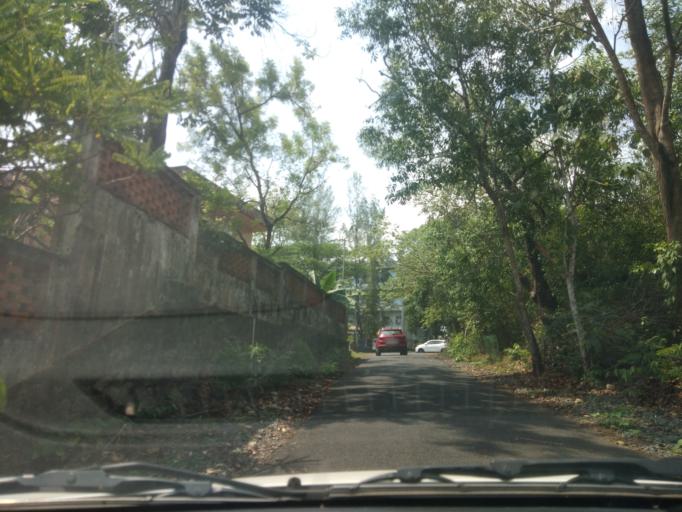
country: IN
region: Kerala
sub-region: Ernakulam
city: Elur
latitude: 10.0441
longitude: 76.3263
